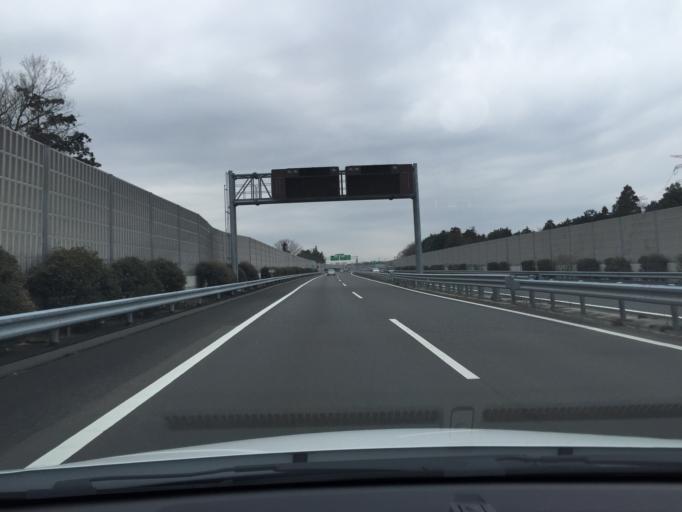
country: JP
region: Saitama
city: Sakado
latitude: 35.9405
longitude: 139.4111
